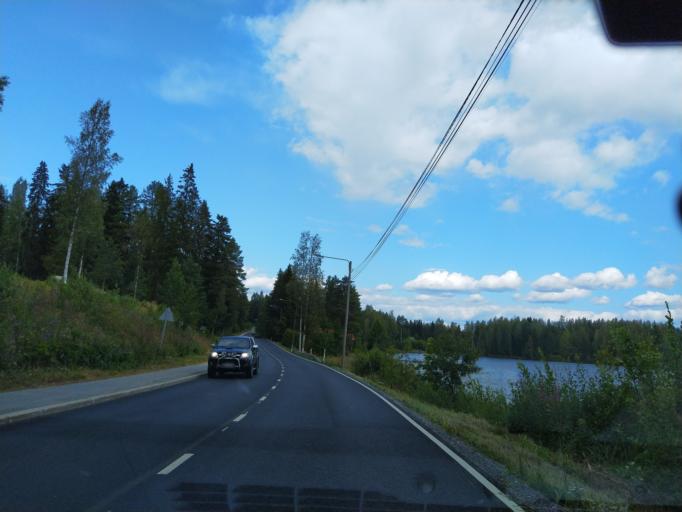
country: FI
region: Pirkanmaa
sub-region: Tampere
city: Kuru
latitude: 61.8872
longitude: 23.7385
